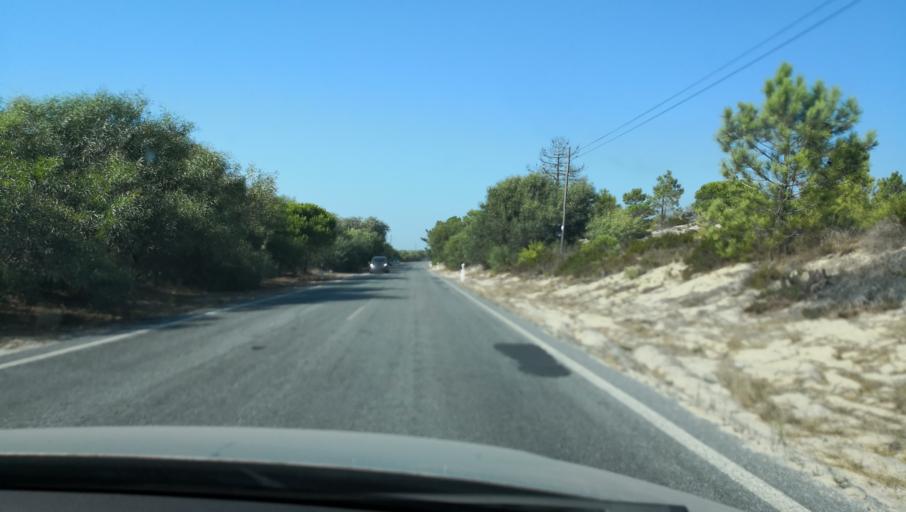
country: PT
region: Setubal
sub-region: Setubal
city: Setubal
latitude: 38.3949
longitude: -8.8041
